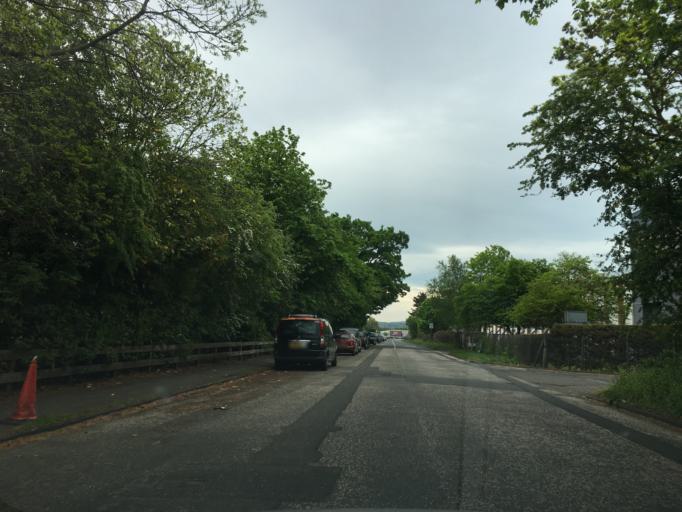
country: GB
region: Scotland
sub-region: Edinburgh
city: Currie
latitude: 55.9431
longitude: -3.3198
